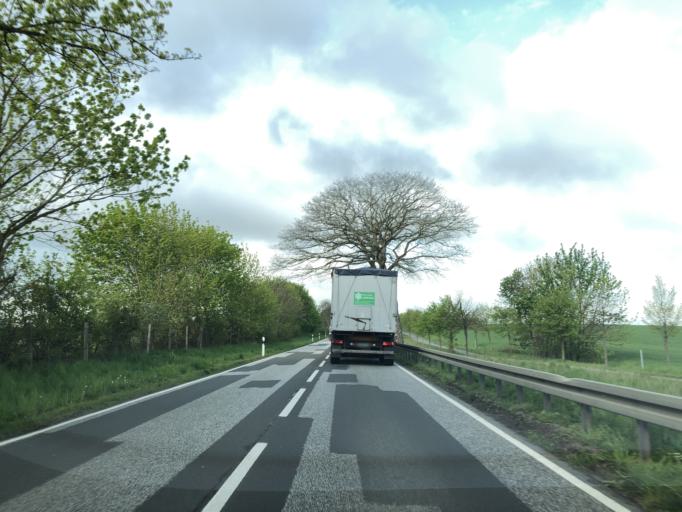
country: DE
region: Mecklenburg-Vorpommern
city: Guestrow
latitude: 53.7715
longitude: 12.1623
